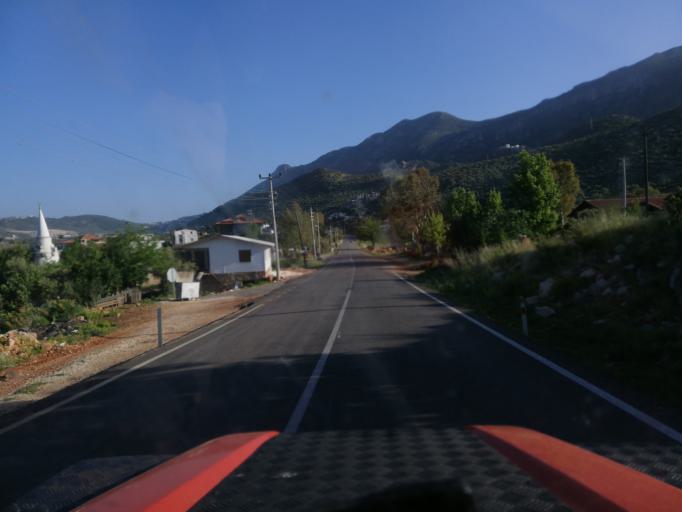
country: TR
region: Antalya
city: Kalkan
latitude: 36.2404
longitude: 29.4275
